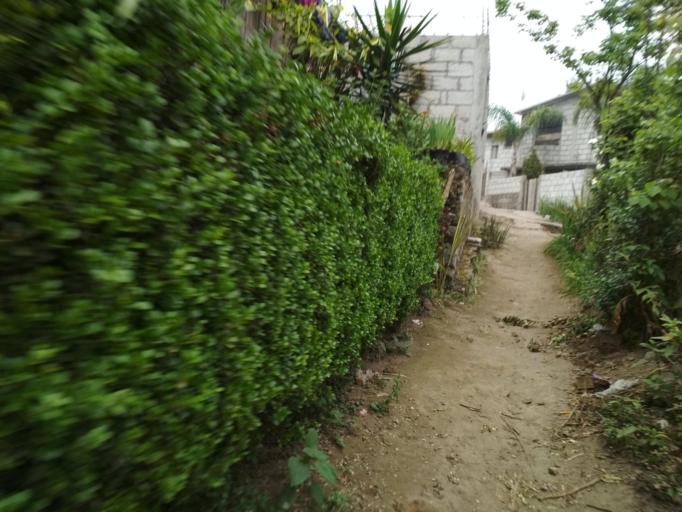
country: MX
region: Veracruz
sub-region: Mariano Escobedo
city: San Isidro el Berro
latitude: 18.9536
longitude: -97.1754
